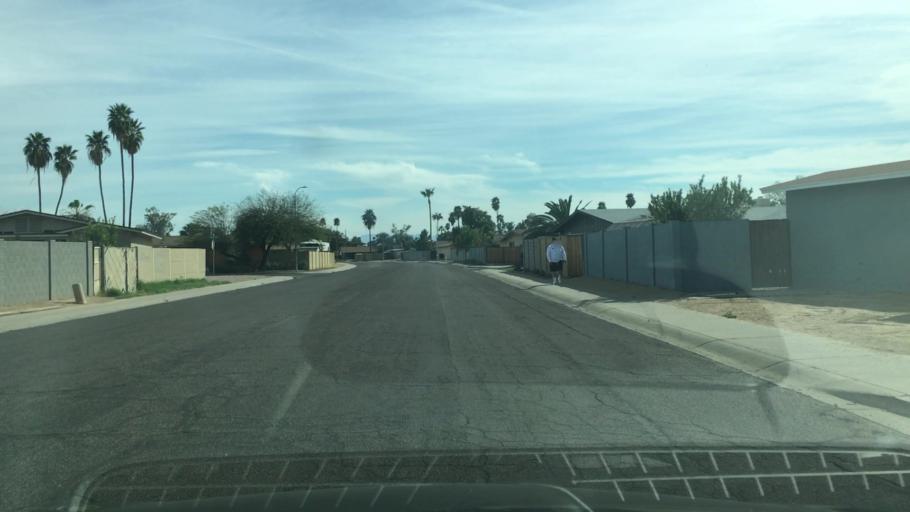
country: US
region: Arizona
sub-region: Maricopa County
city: Glendale
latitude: 33.5729
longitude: -112.1563
